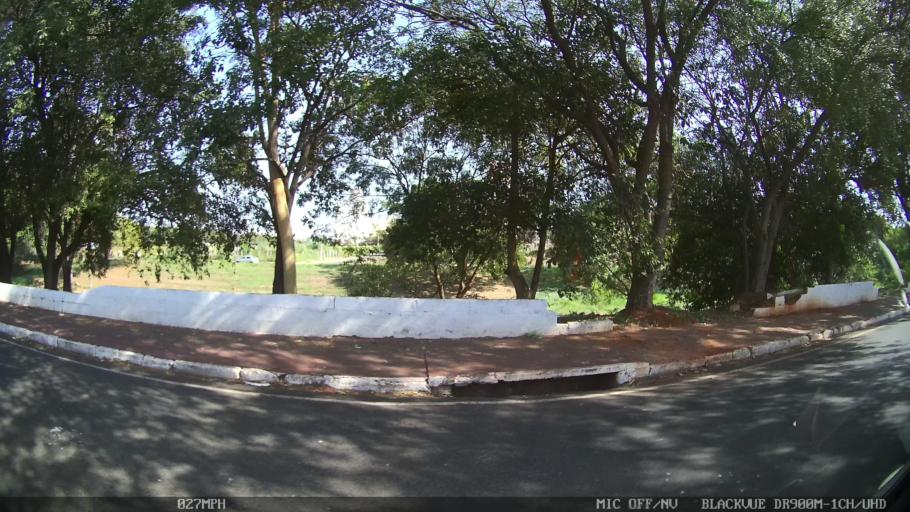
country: BR
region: Sao Paulo
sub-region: Sao Jose Do Rio Preto
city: Sao Jose do Rio Preto
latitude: -20.7958
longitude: -49.4015
